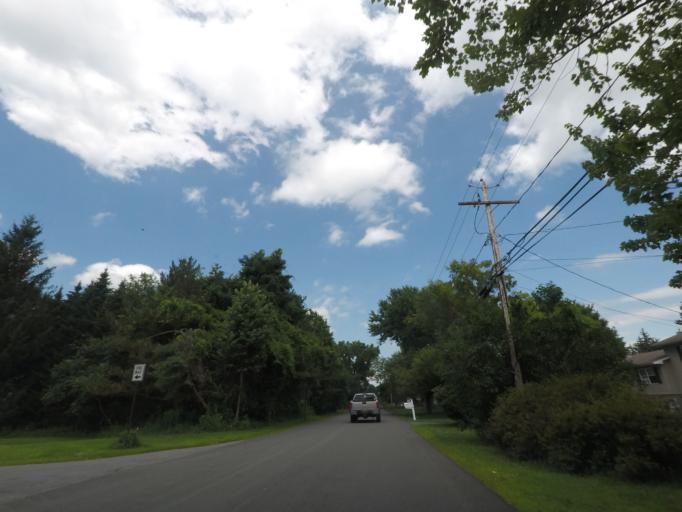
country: US
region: New York
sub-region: Rensselaer County
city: Castleton-on-Hudson
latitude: 42.5292
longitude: -73.6906
